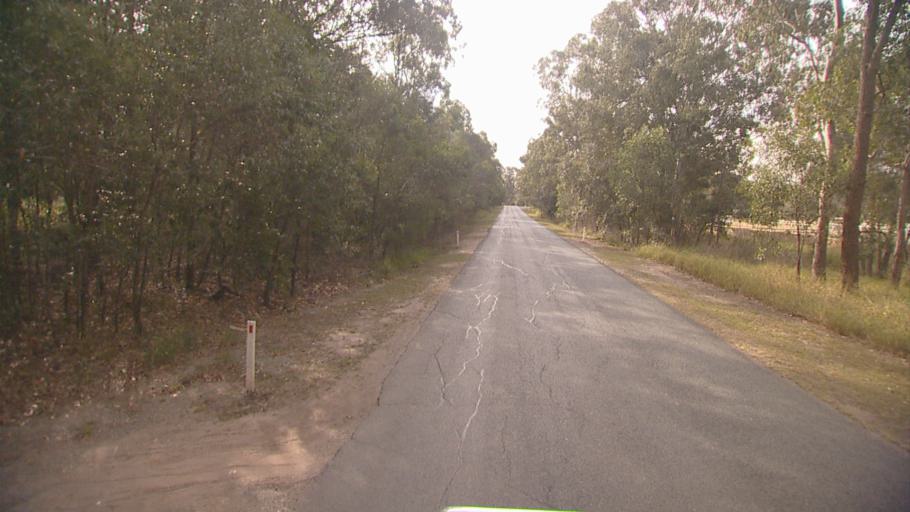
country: AU
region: Queensland
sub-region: Logan
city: Chambers Flat
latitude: -27.7696
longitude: 153.1163
